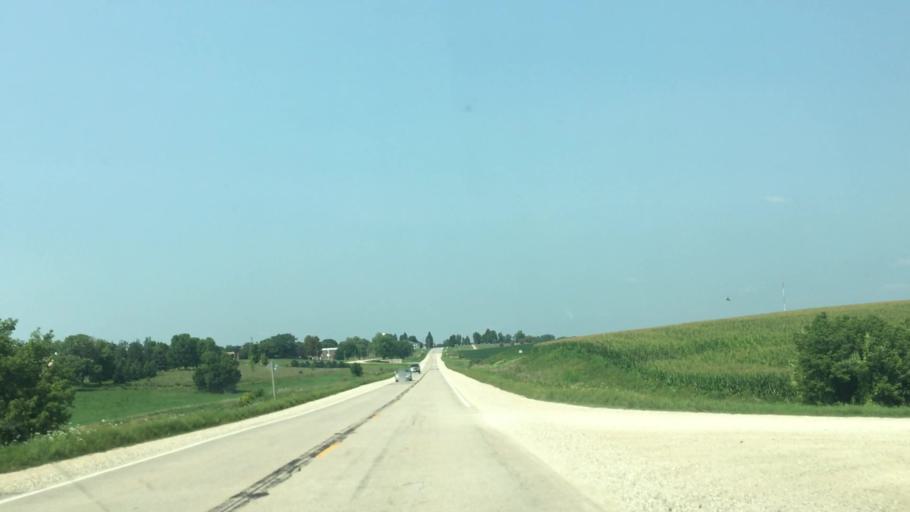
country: US
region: Iowa
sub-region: Winneshiek County
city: Decorah
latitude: 43.1689
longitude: -91.8644
